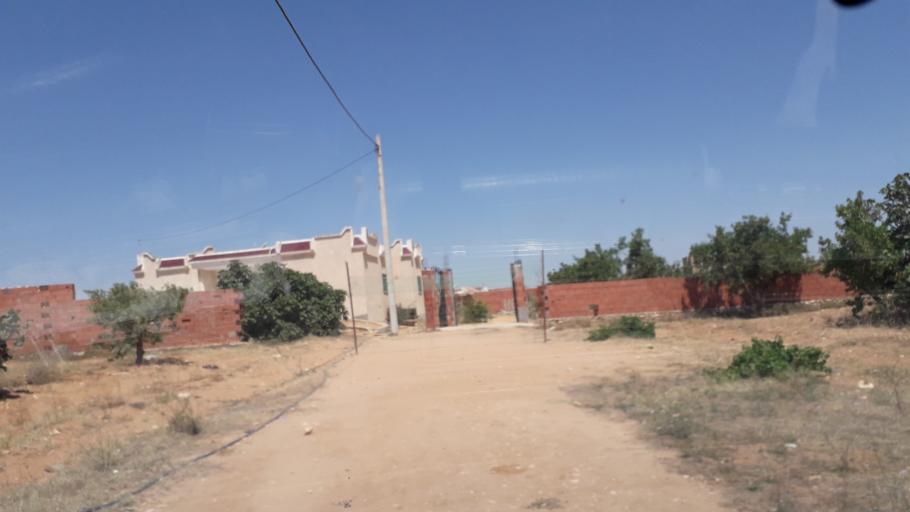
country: TN
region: Safaqis
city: Al Qarmadah
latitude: 34.8252
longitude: 10.7670
